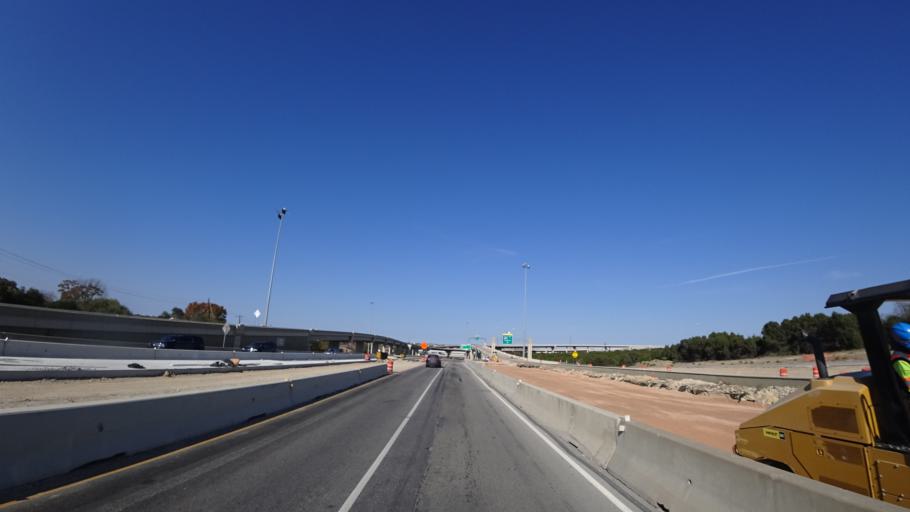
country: US
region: Texas
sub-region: Travis County
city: Austin
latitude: 30.3210
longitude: -97.6670
